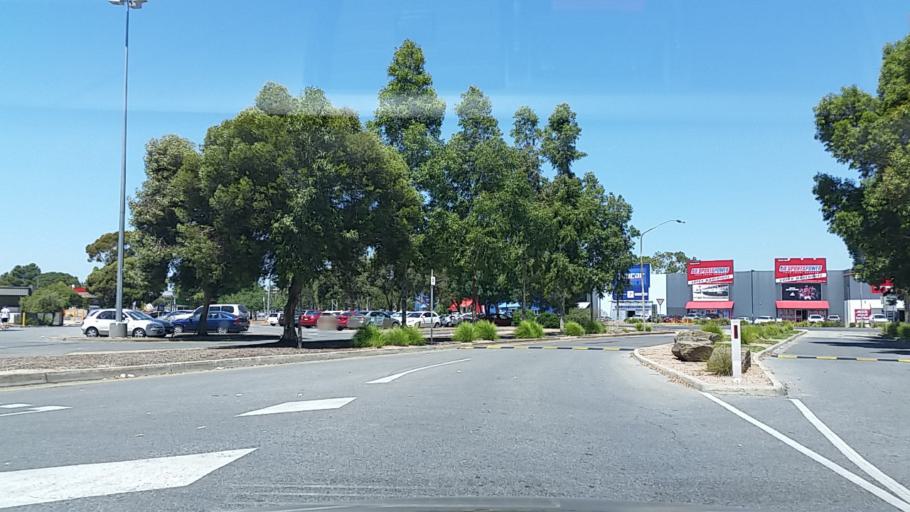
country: AU
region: South Australia
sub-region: Salisbury
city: Elizabeth
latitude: -34.7199
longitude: 138.6693
